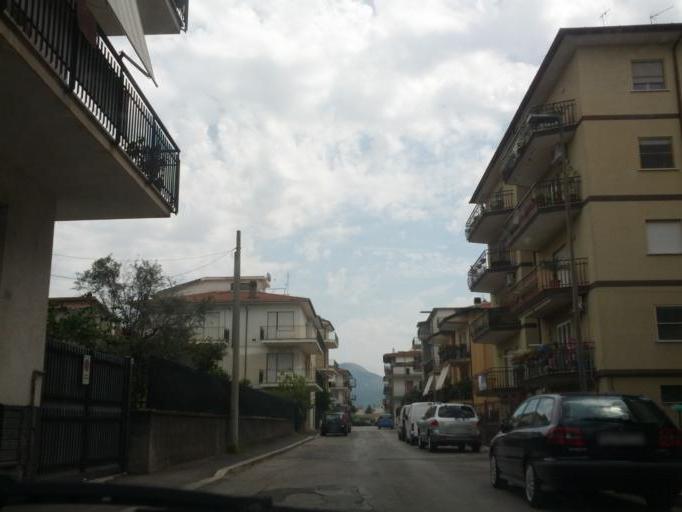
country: IT
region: Latium
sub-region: Provincia di Latina
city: Fondi
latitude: 41.3512
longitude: 13.4309
